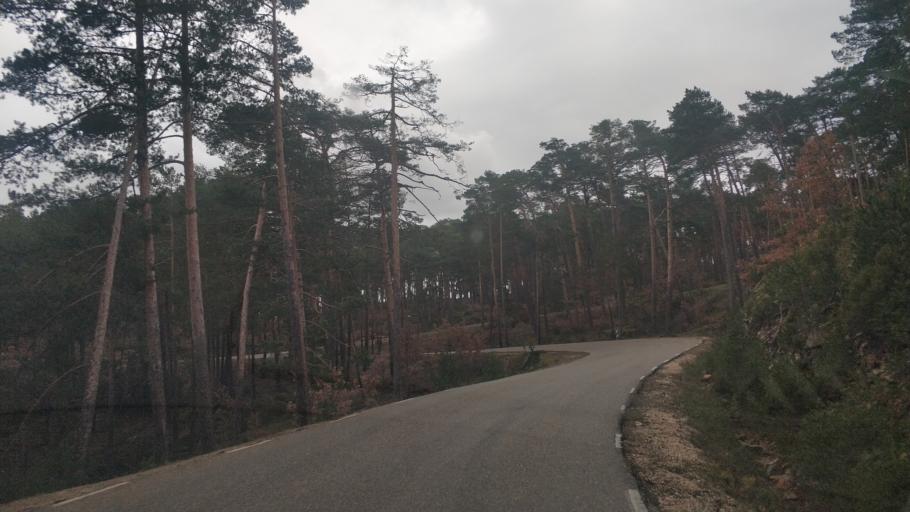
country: ES
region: Castille and Leon
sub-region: Provincia de Burgos
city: Canicosa de la Sierra
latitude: 41.9181
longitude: -3.0378
